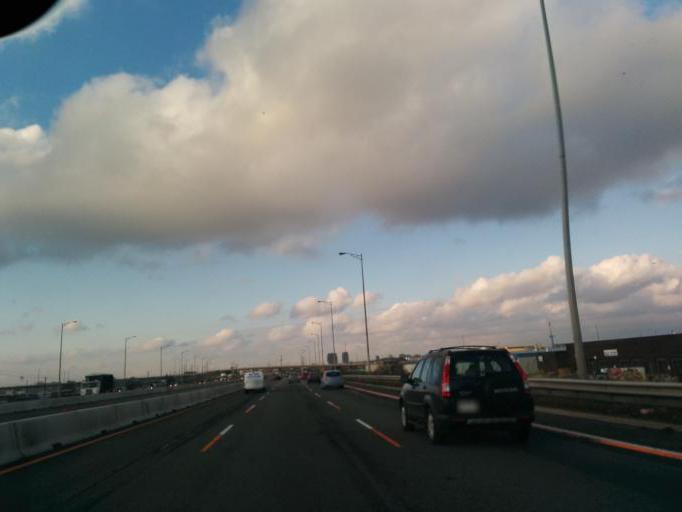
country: CA
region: Ontario
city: Etobicoke
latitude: 43.6897
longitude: -79.6029
